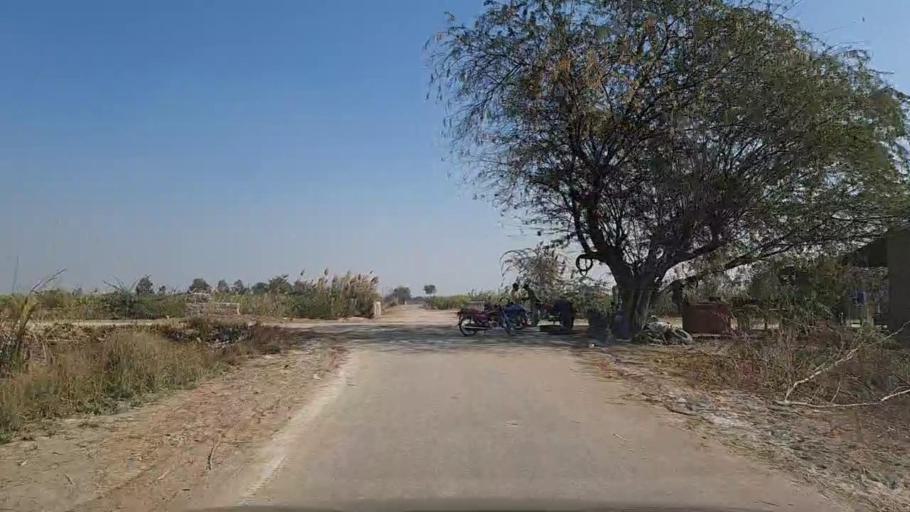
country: PK
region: Sindh
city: Bandhi
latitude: 26.5558
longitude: 68.3525
